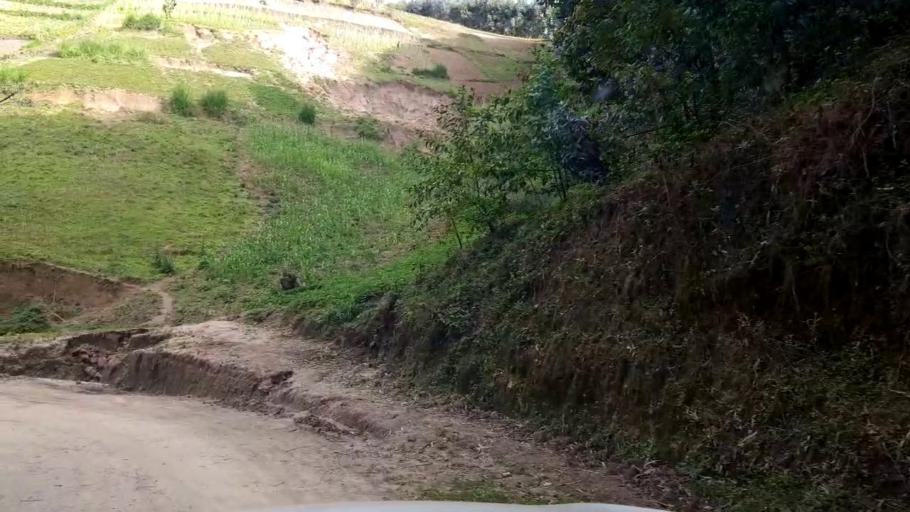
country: RW
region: Western Province
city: Kibuye
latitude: -1.8664
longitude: 29.5460
